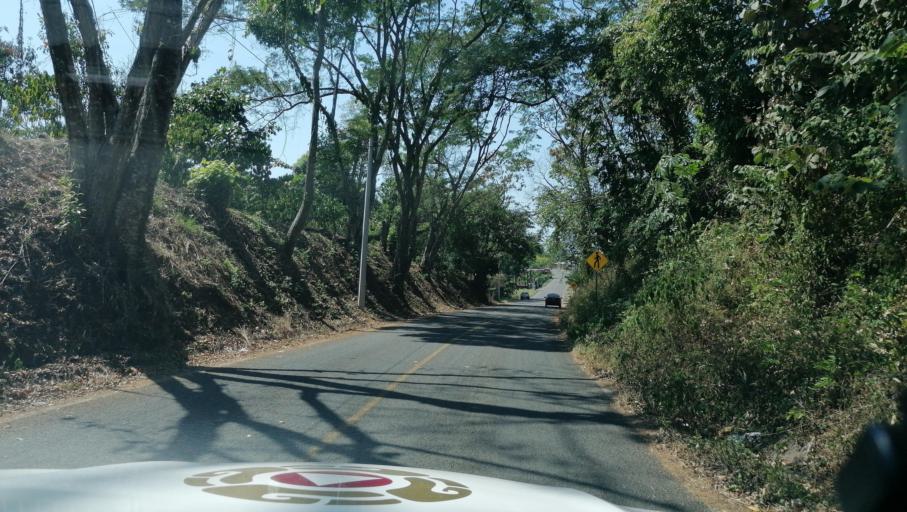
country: MX
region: Chiapas
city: Veinte de Noviembre
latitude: 14.9999
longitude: -92.2316
